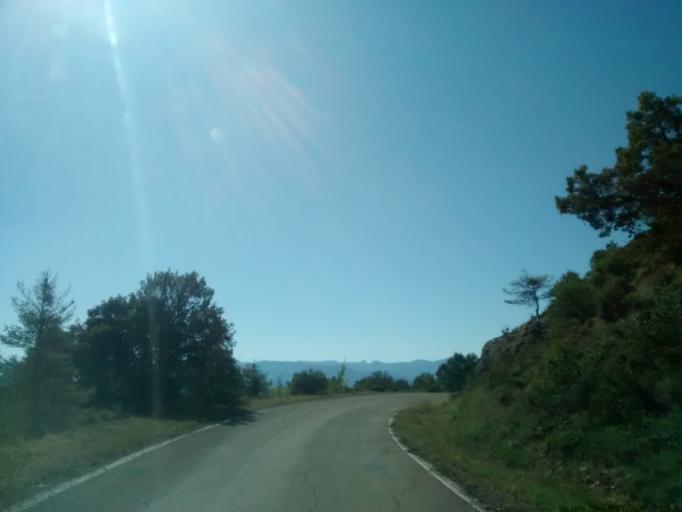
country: ES
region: Aragon
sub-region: Provincia de Huesca
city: Jaca
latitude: 42.4829
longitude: -0.5677
